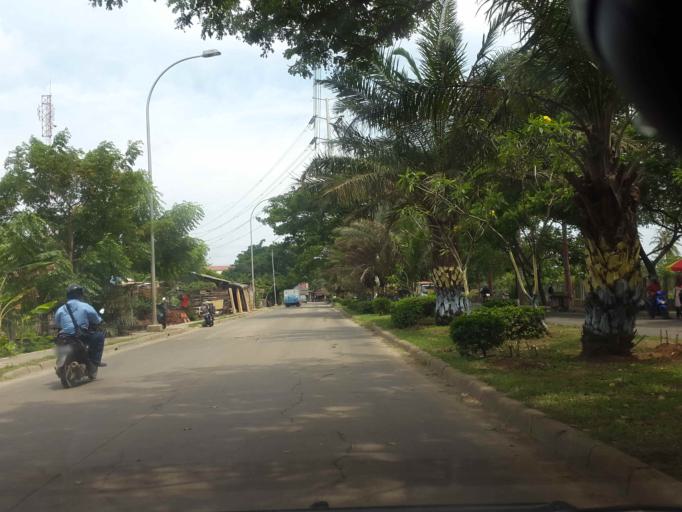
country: ID
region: Banten
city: Tangerang
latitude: -6.1541
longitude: 106.6549
